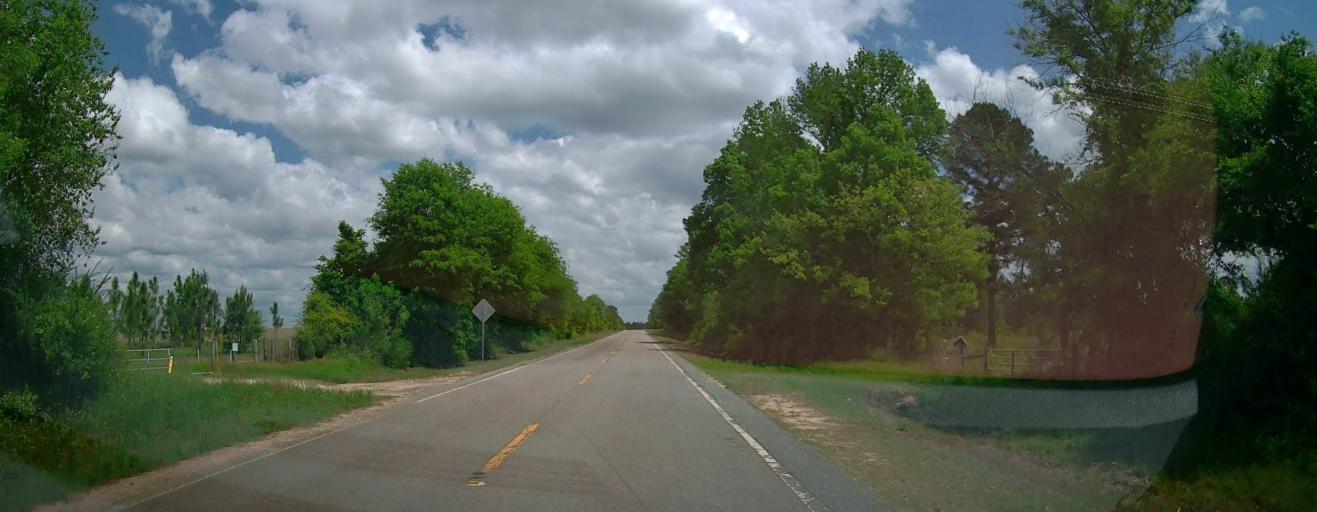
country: US
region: Georgia
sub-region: Dodge County
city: Chester
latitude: 32.5280
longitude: -83.2075
